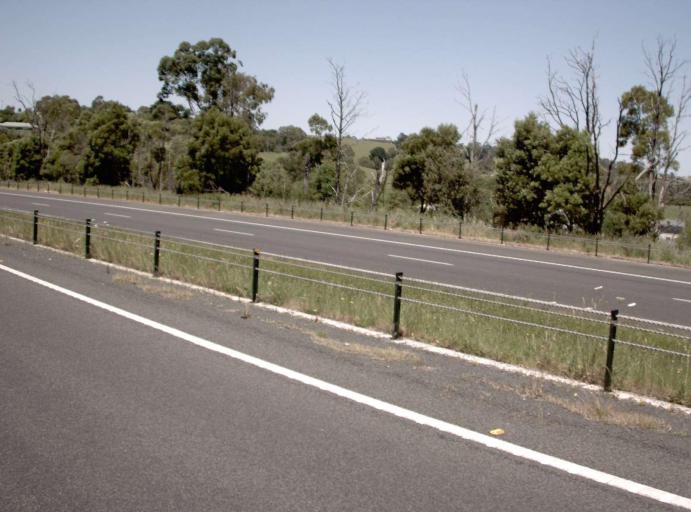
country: AU
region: Victoria
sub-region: Baw Baw
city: Warragul
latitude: -38.1682
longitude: 145.9170
